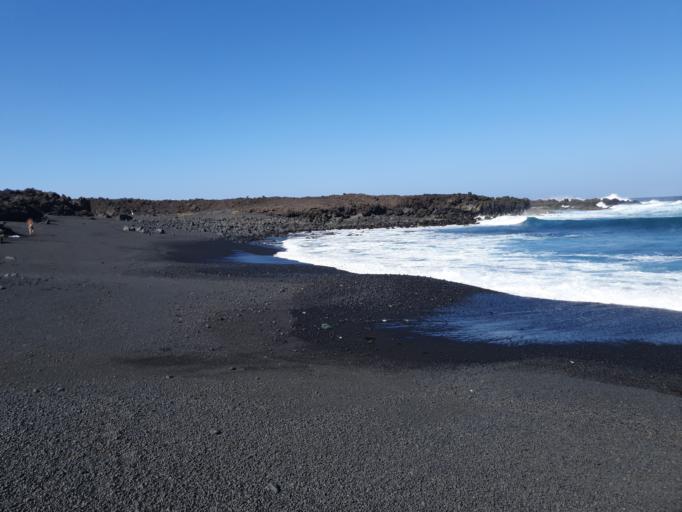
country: ES
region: Canary Islands
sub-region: Provincia de Las Palmas
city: Tinajo
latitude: 29.0637
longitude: -13.7667
